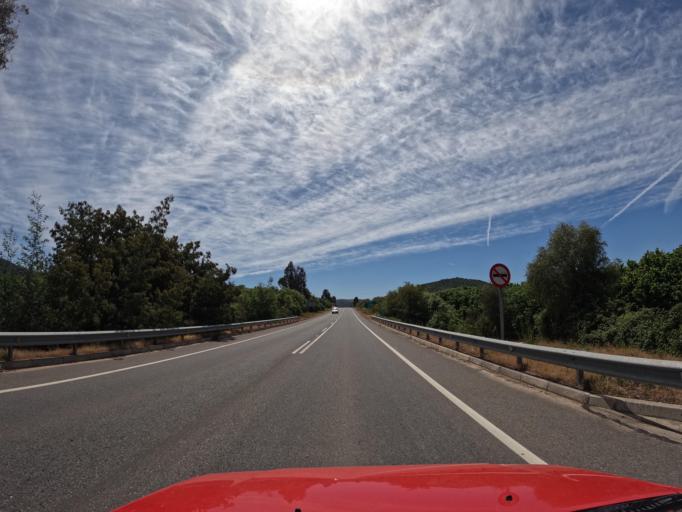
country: CL
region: Maule
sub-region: Provincia de Talca
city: Talca
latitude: -35.2702
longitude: -71.5400
